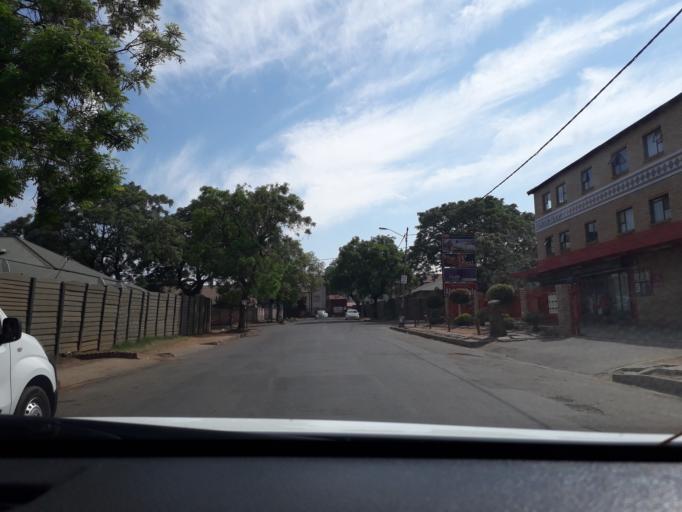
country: ZA
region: Gauteng
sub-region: City of Johannesburg Metropolitan Municipality
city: Modderfontein
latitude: -26.1024
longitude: 28.2356
